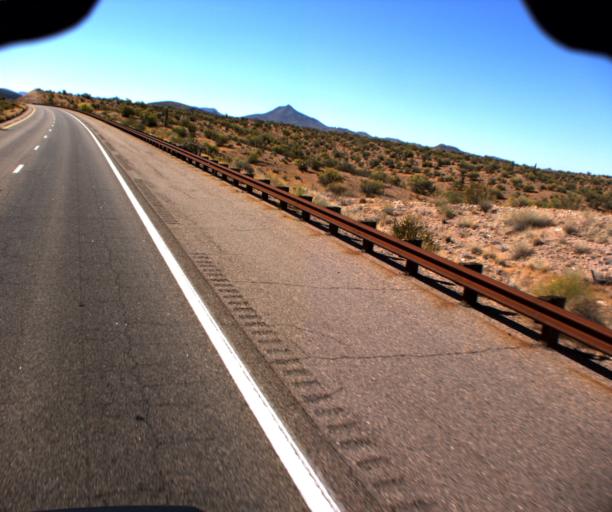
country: US
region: Arizona
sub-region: Yavapai County
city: Bagdad
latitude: 34.5972
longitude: -113.5174
